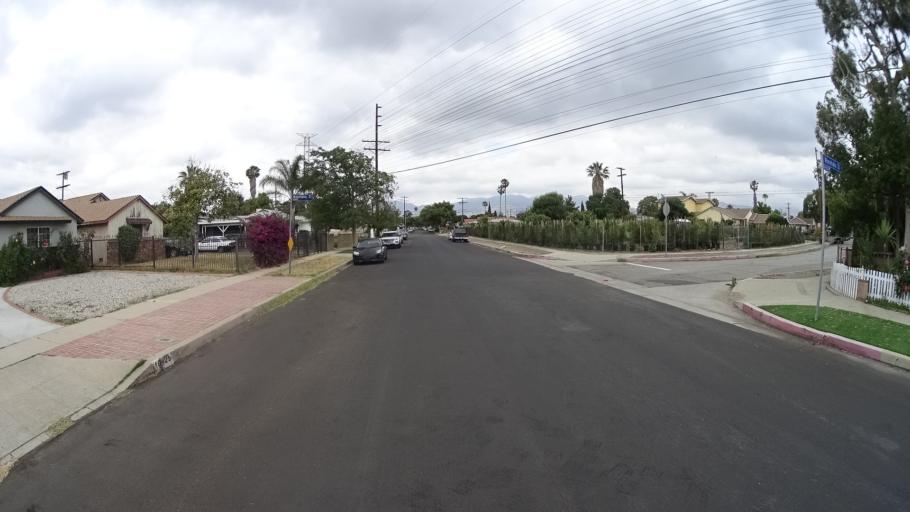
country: US
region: California
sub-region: Los Angeles County
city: San Fernando
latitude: 34.2596
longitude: -118.4531
